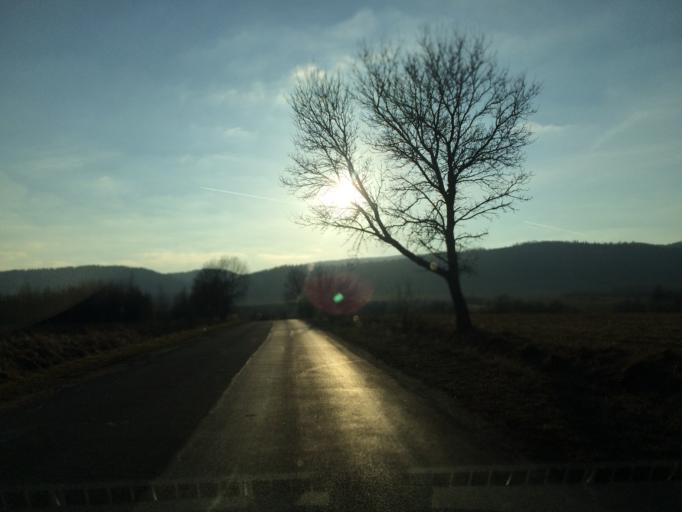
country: PL
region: Lower Silesian Voivodeship
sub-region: Powiat klodzki
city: Miedzylesie
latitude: 50.2059
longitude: 16.6473
